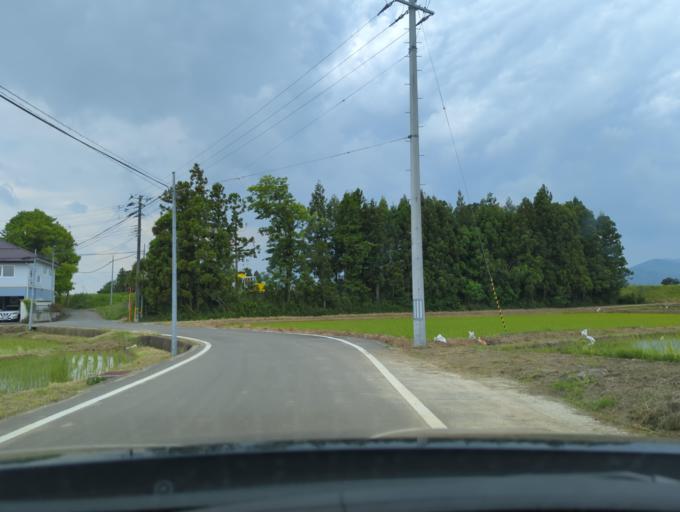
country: JP
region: Fukushima
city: Koriyama
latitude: 37.3737
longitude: 140.3000
